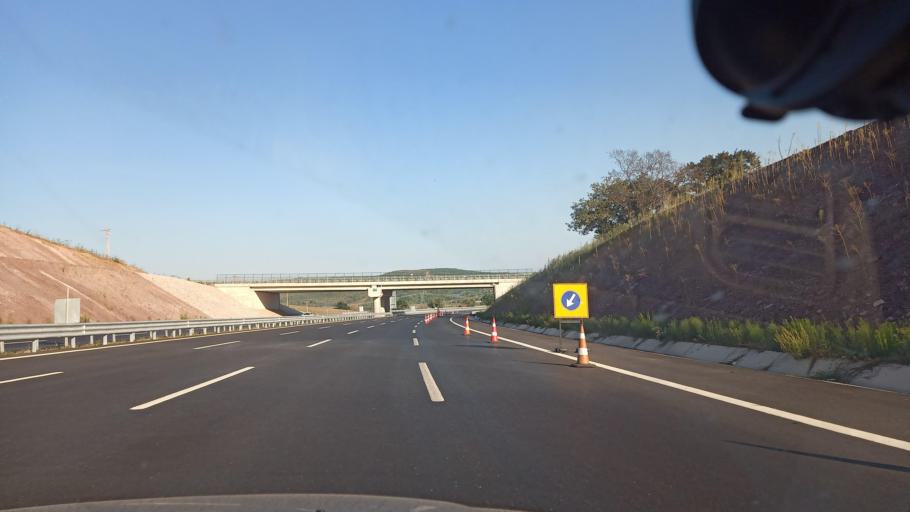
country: TR
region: Sakarya
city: Adapazari
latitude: 40.8385
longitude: 30.3801
